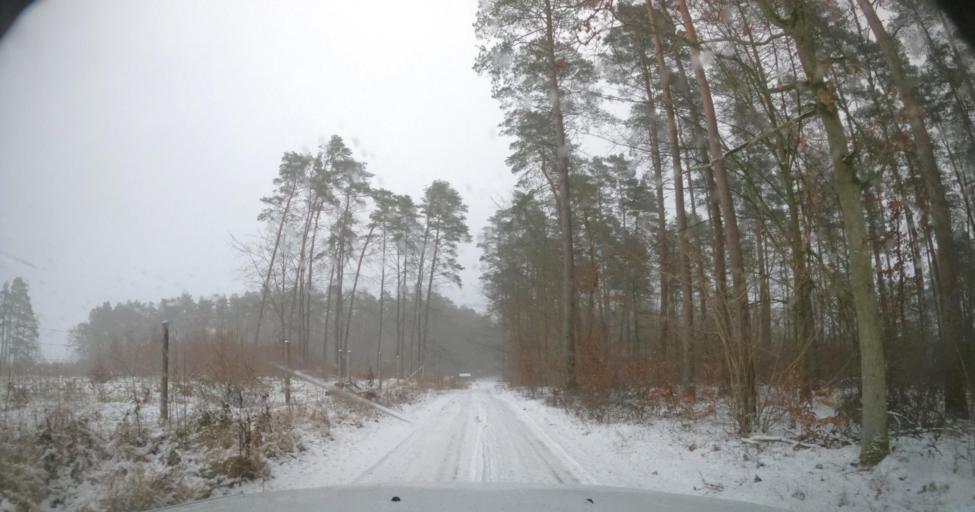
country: PL
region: West Pomeranian Voivodeship
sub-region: Powiat kamienski
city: Golczewo
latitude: 53.7713
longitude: 14.9385
